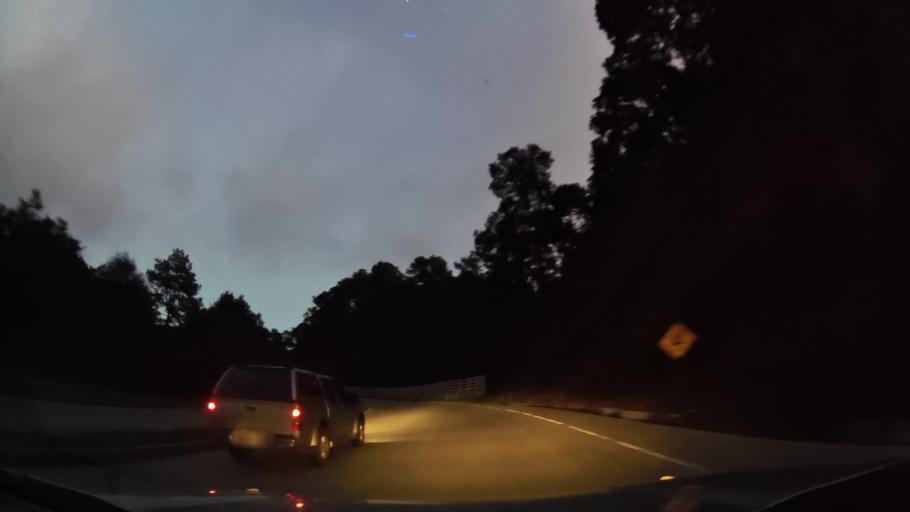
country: GT
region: Chimaltenango
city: Santa Apolonia
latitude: 14.7981
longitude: -90.9861
